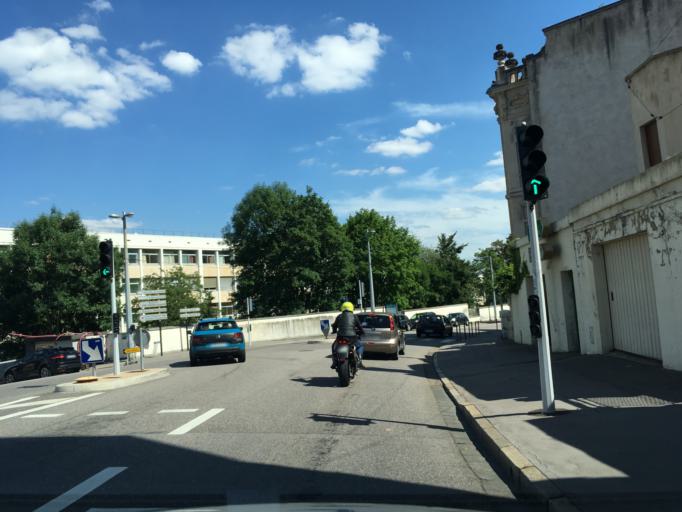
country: FR
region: Lorraine
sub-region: Departement de Meurthe-et-Moselle
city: Maxeville
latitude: 48.6958
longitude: 6.1645
